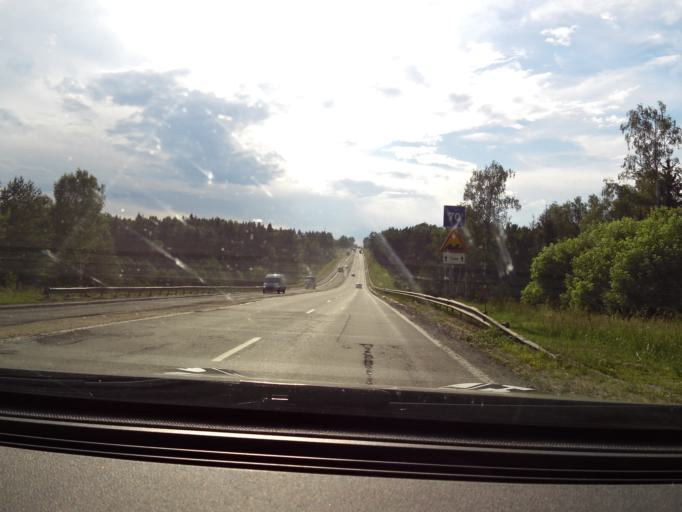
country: RU
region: Vladimir
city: Gorokhovets
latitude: 56.1676
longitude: 42.4604
